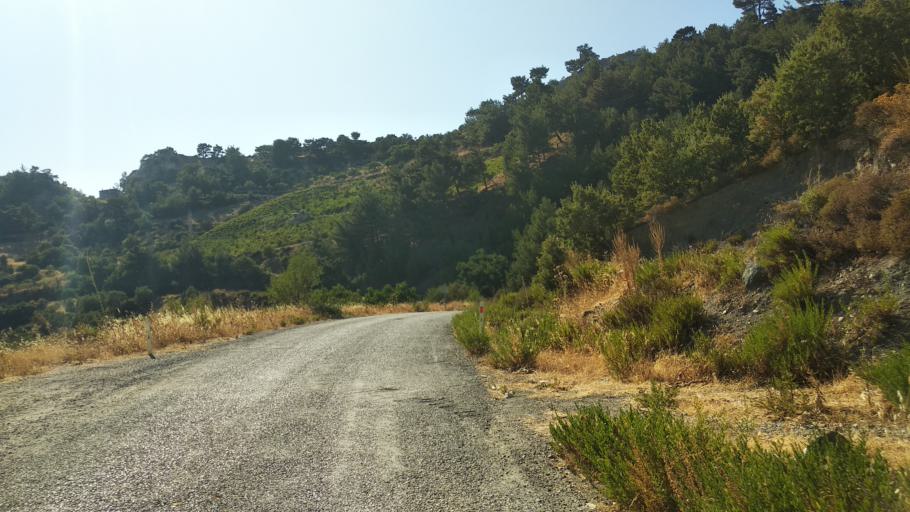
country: TR
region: Izmir
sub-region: Seferihisar
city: Seferhisar
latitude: 38.3221
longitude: 26.9334
